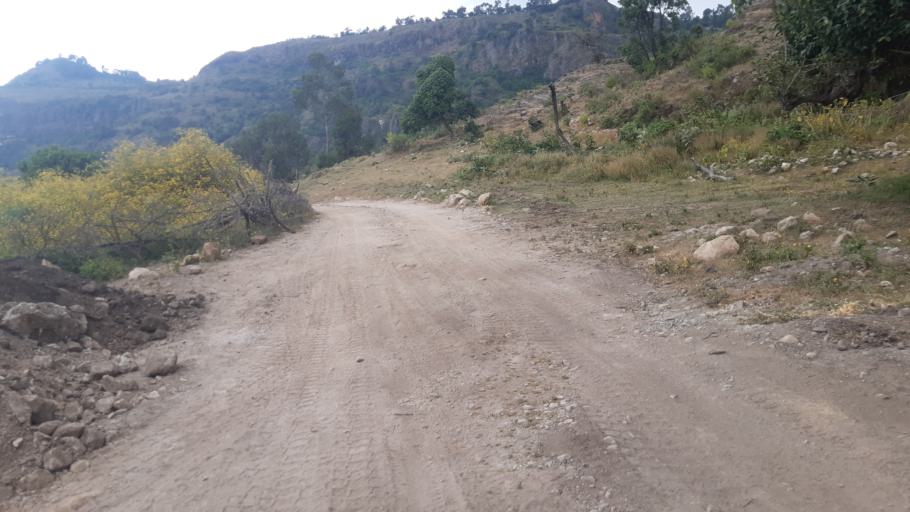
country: ET
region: Amhara
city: Dabat
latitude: 13.3416
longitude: 37.4043
